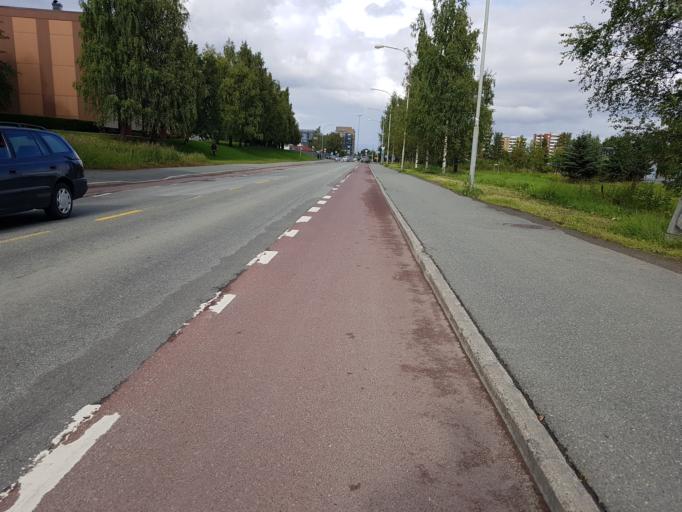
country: NO
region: Sor-Trondelag
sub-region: Trondheim
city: Trondheim
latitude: 63.4184
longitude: 10.4352
